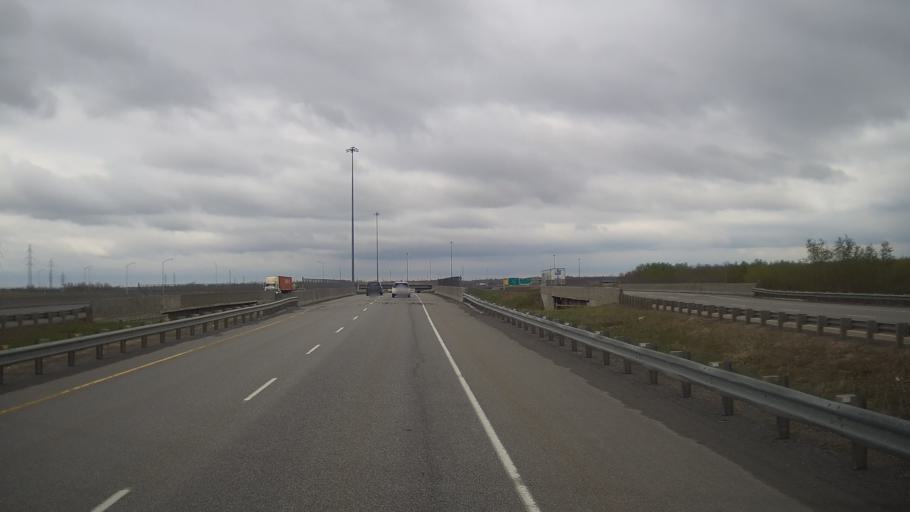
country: CA
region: Quebec
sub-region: Monteregie
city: Vaudreuil-Dorion
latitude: 45.3664
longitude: -74.0501
